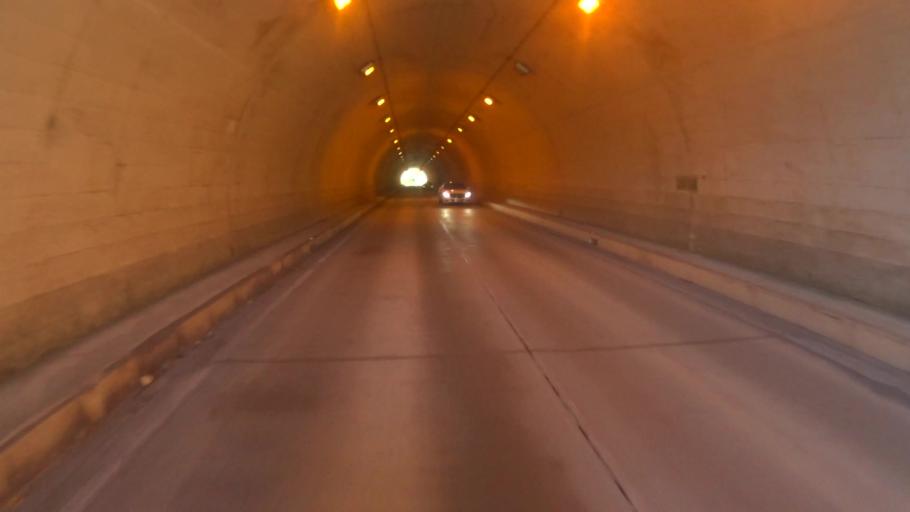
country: JP
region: Kyoto
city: Miyazu
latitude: 35.6769
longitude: 135.2928
